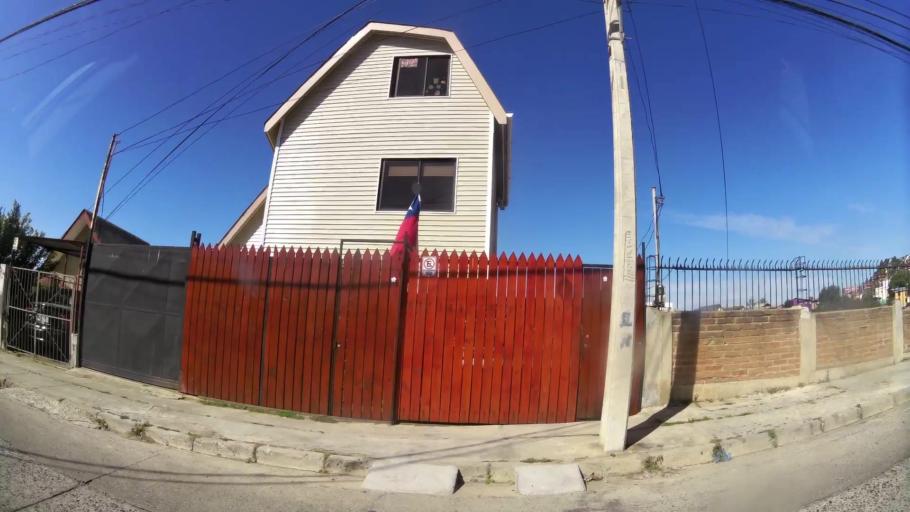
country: CL
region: Valparaiso
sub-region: Provincia de Valparaiso
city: Vina del Mar
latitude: -33.0329
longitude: -71.5630
